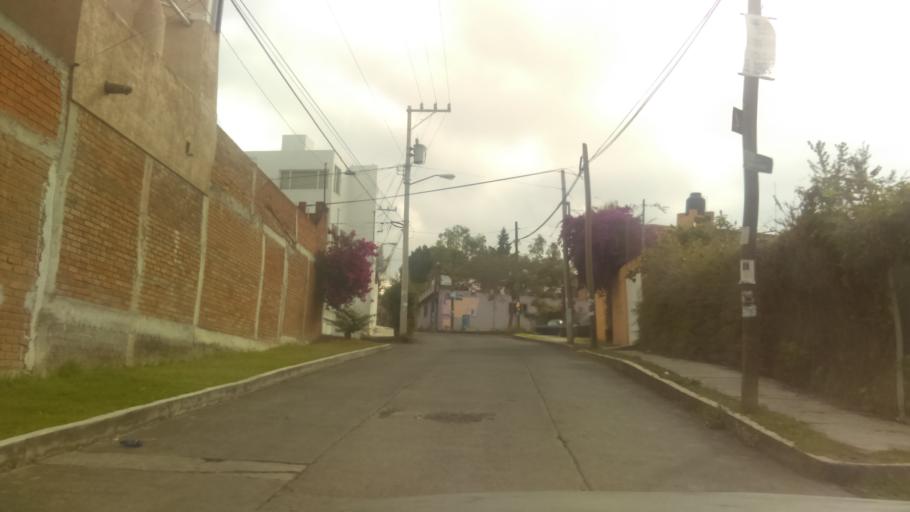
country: MX
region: Michoacan
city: Morelia
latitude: 19.6726
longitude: -101.1955
